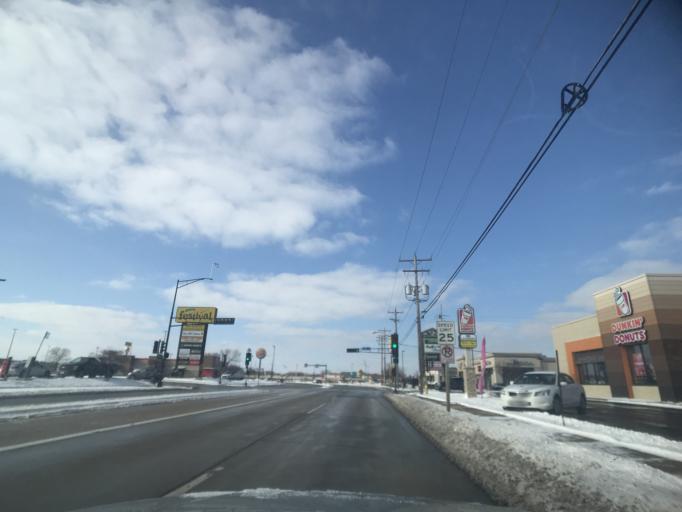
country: US
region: Wisconsin
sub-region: Brown County
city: De Pere
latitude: 44.4512
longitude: -88.0853
